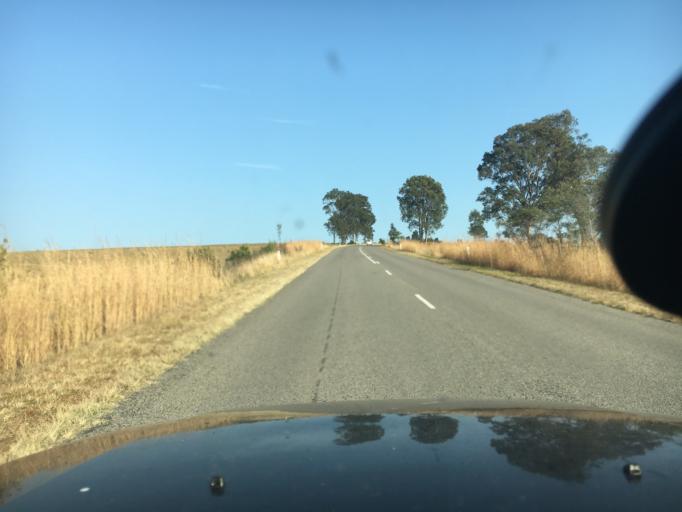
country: AU
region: New South Wales
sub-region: Cessnock
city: Branxton
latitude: -32.5836
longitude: 151.3248
